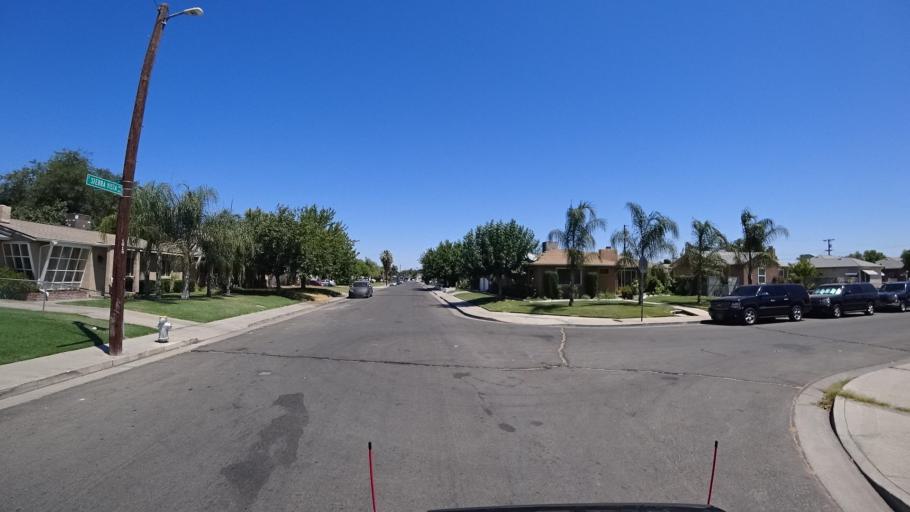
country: US
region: California
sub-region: Fresno County
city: Fresno
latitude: 36.7408
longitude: -119.7416
